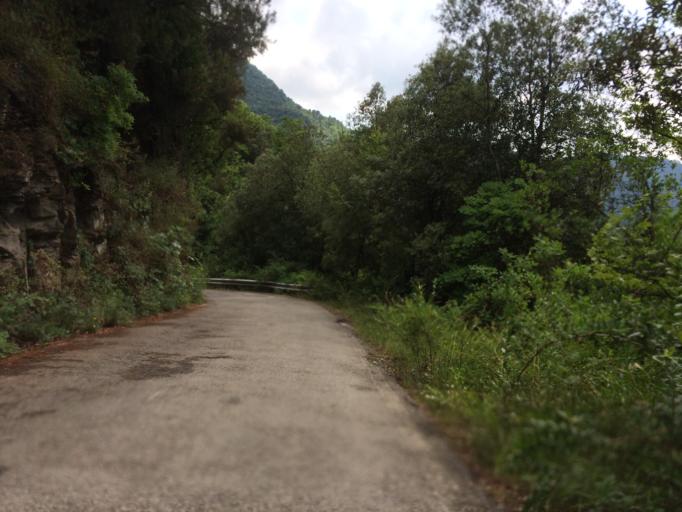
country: IT
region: Liguria
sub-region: Provincia di Imperia
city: Castel Vittorio
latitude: 43.9405
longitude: 7.6849
